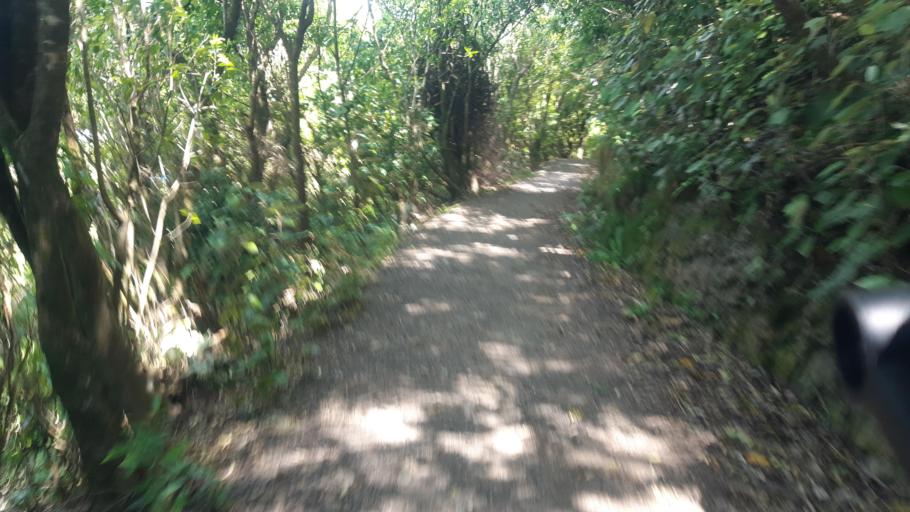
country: NZ
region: Marlborough
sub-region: Marlborough District
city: Picton
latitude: -41.2700
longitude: 174.0309
